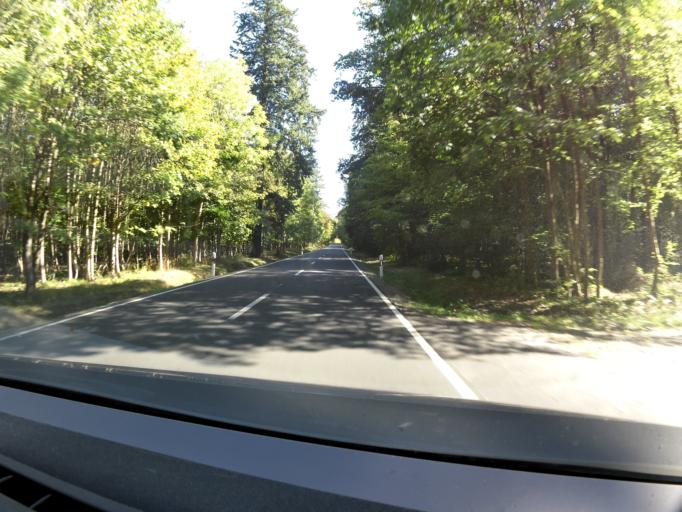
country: DE
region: Saxony-Anhalt
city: Hasselfelde
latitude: 51.6782
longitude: 10.9171
